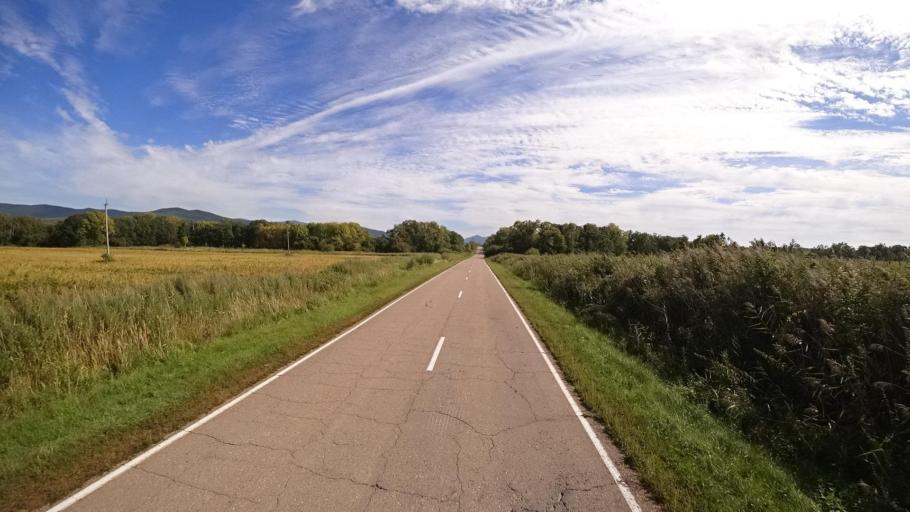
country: RU
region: Primorskiy
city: Yakovlevka
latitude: 44.4215
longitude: 133.5783
